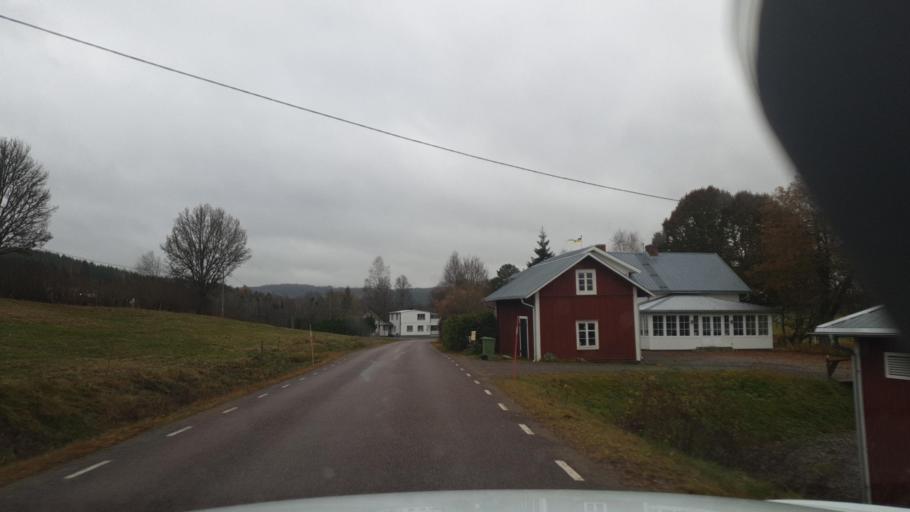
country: SE
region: Vaermland
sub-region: Eda Kommun
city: Charlottenberg
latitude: 59.9676
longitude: 12.4080
